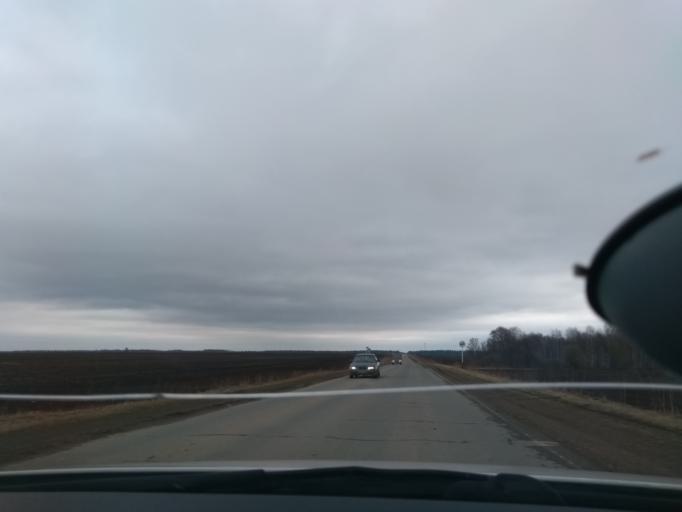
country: RU
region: Perm
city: Kungur
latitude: 57.3793
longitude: 56.8484
